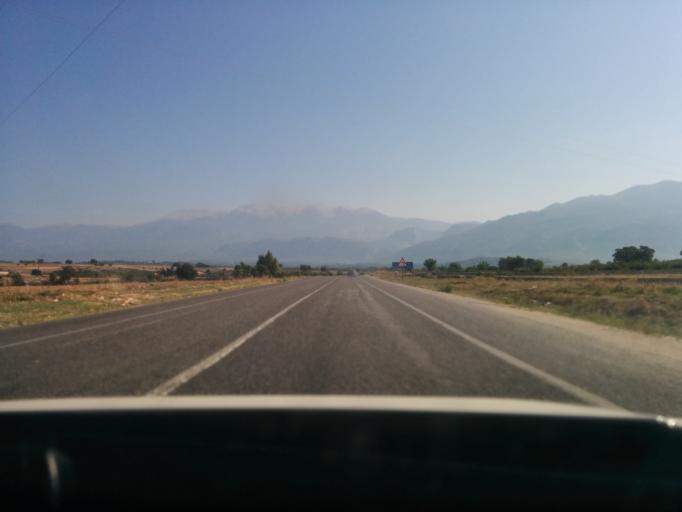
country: TR
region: Mugla
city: Esen
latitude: 36.4435
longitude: 29.2847
